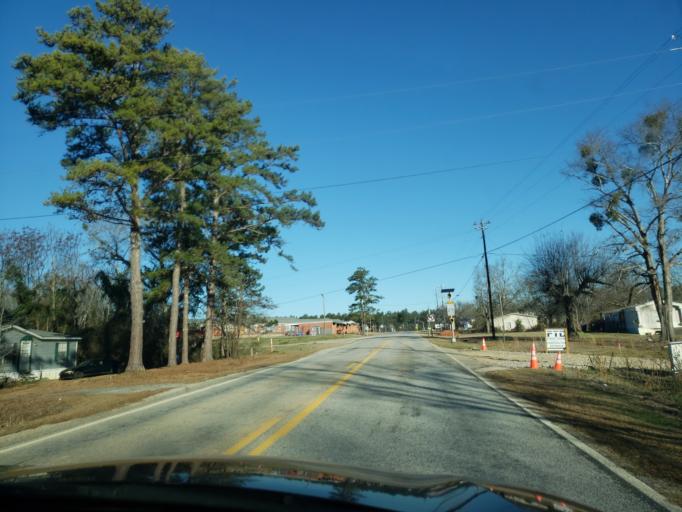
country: US
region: Alabama
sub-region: Elmore County
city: Tallassee
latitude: 32.6007
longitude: -85.8030
